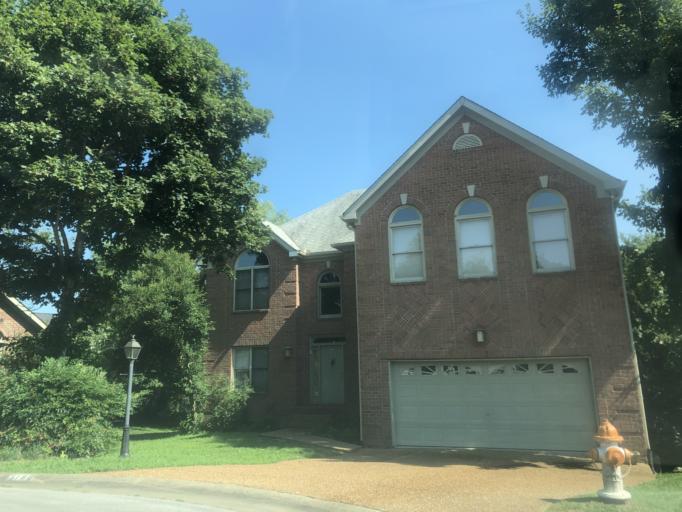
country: US
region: Tennessee
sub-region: Wilson County
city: Green Hill
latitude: 36.1501
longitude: -86.5907
